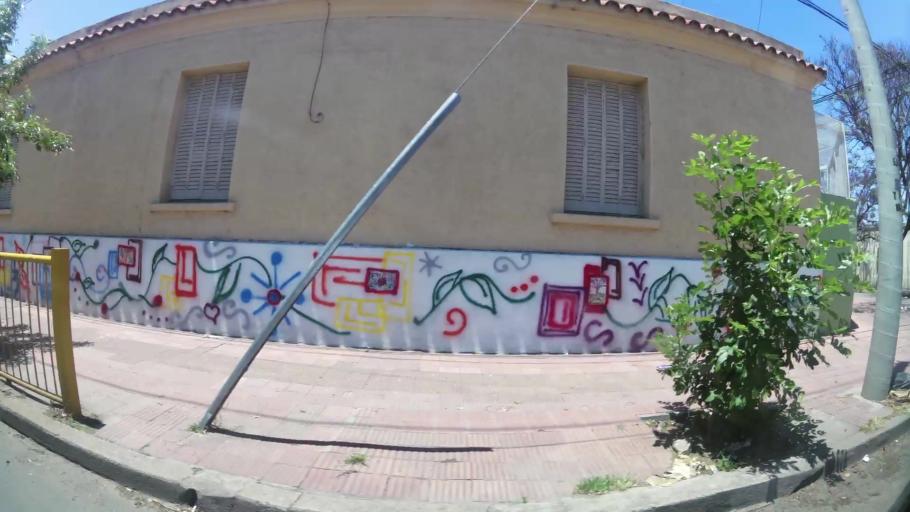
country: AR
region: Cordoba
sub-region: Departamento de Capital
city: Cordoba
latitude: -31.3955
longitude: -64.2137
